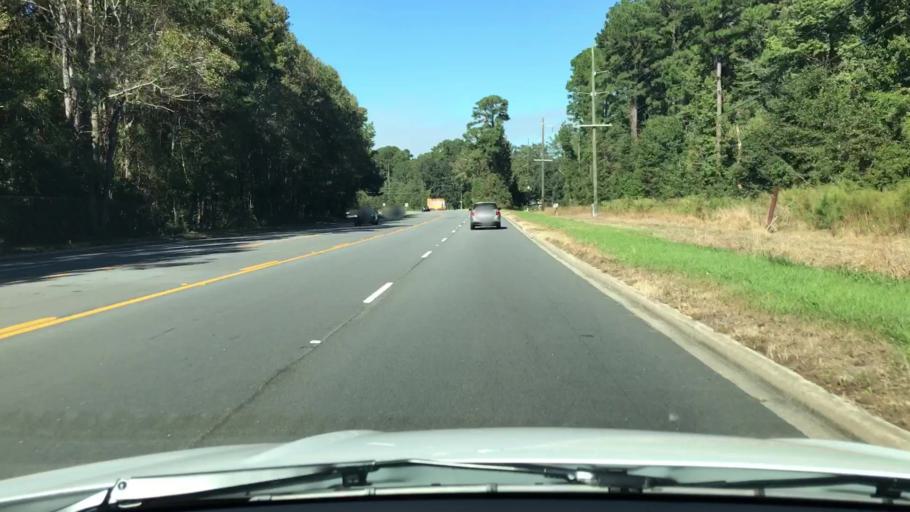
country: US
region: South Carolina
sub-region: Beaufort County
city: Laurel Bay
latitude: 32.5827
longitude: -80.7430
